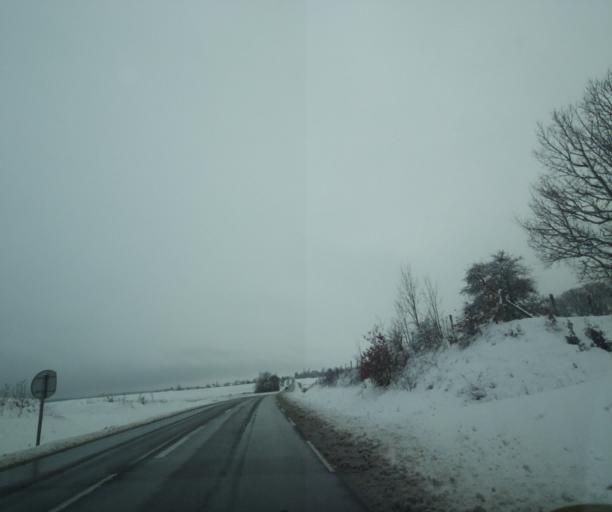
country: FR
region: Champagne-Ardenne
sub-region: Departement de la Haute-Marne
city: Montier-en-Der
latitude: 48.5286
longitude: 4.8154
